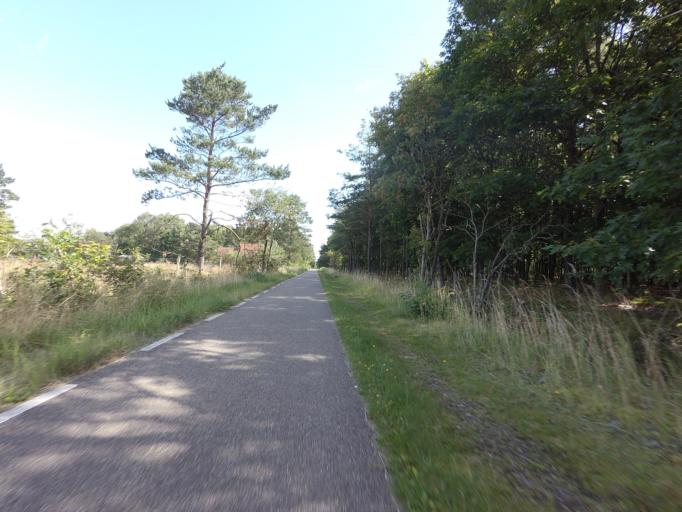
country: DK
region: Central Jutland
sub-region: Silkeborg Kommune
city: Svejbaek
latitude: 56.1730
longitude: 9.6204
